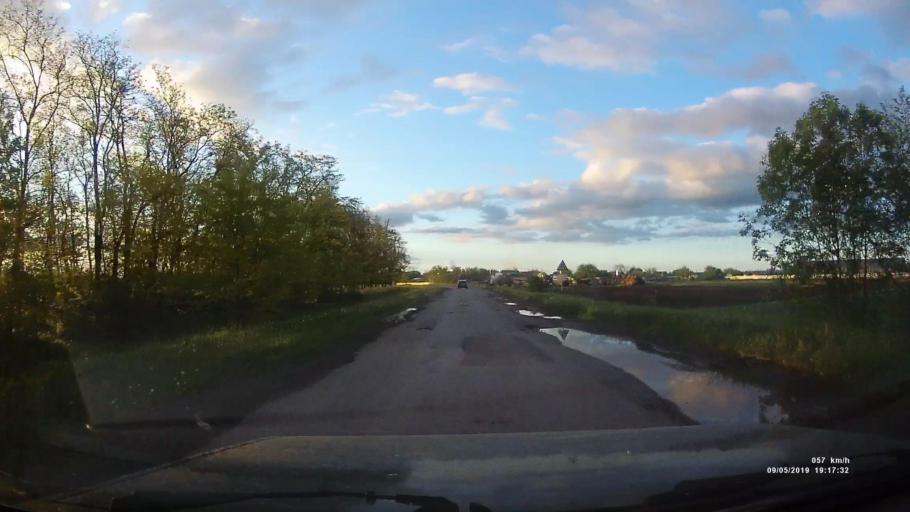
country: RU
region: Krasnodarskiy
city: Kanelovskaya
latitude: 46.7864
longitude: 39.2115
